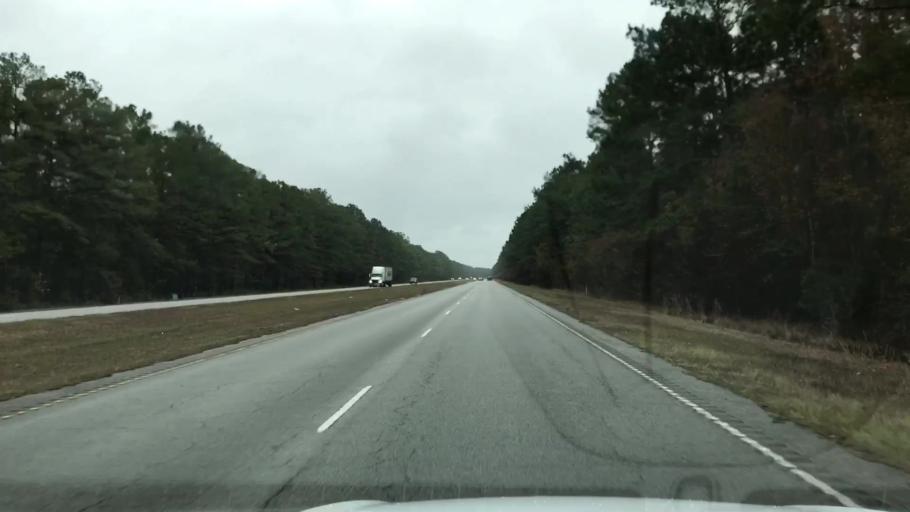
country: US
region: South Carolina
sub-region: Charleston County
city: Awendaw
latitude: 32.9619
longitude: -79.6857
